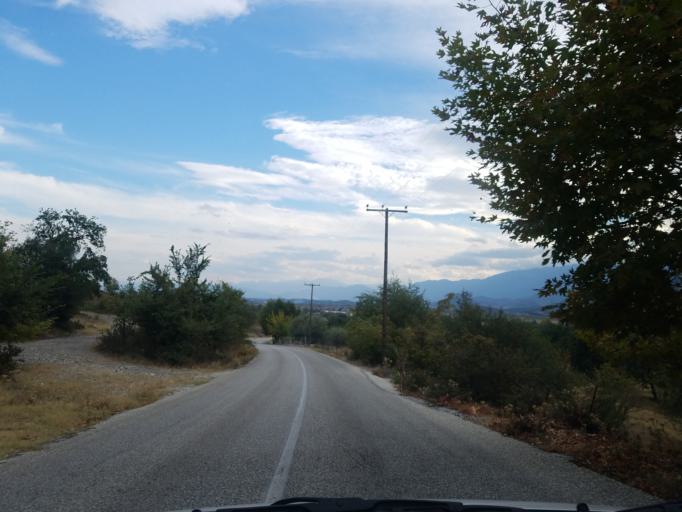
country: GR
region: Thessaly
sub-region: Trikala
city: Kalampaka
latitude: 39.7000
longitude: 21.6493
